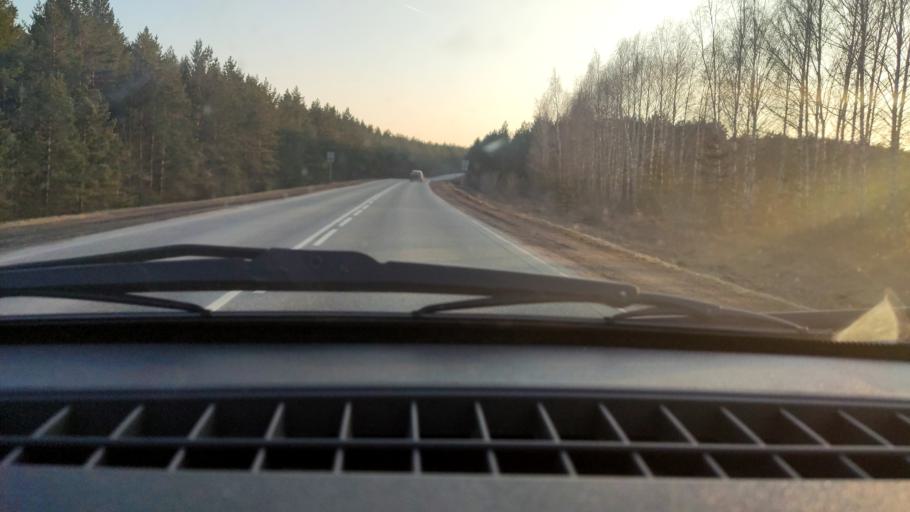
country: RU
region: Bashkortostan
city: Davlekanovo
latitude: 54.2444
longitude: 55.0729
